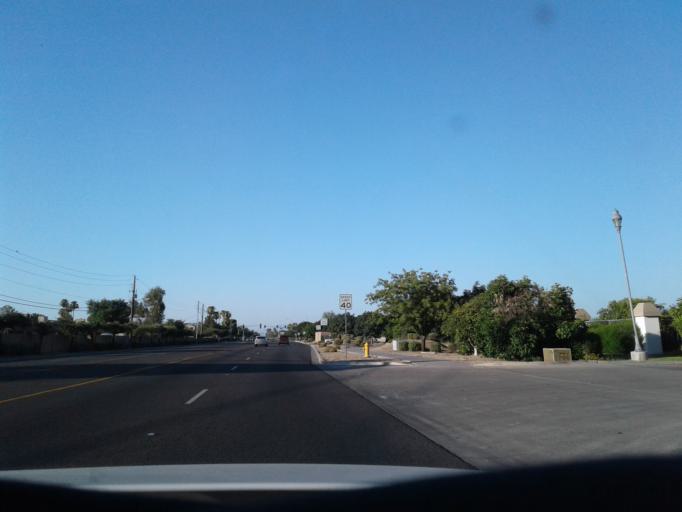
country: US
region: Arizona
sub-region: Maricopa County
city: Glendale
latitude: 33.5740
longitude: -112.1863
